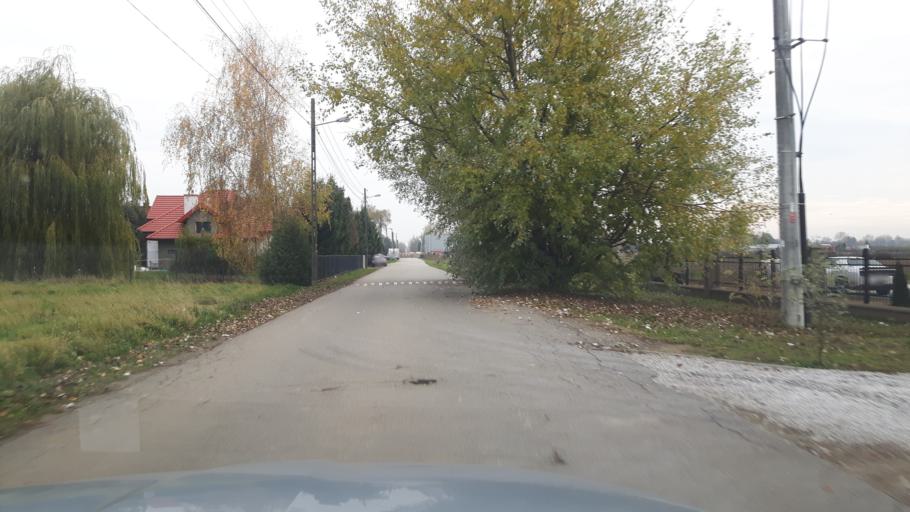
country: PL
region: Masovian Voivodeship
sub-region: Warszawa
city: Wilanow
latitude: 52.1606
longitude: 21.1257
